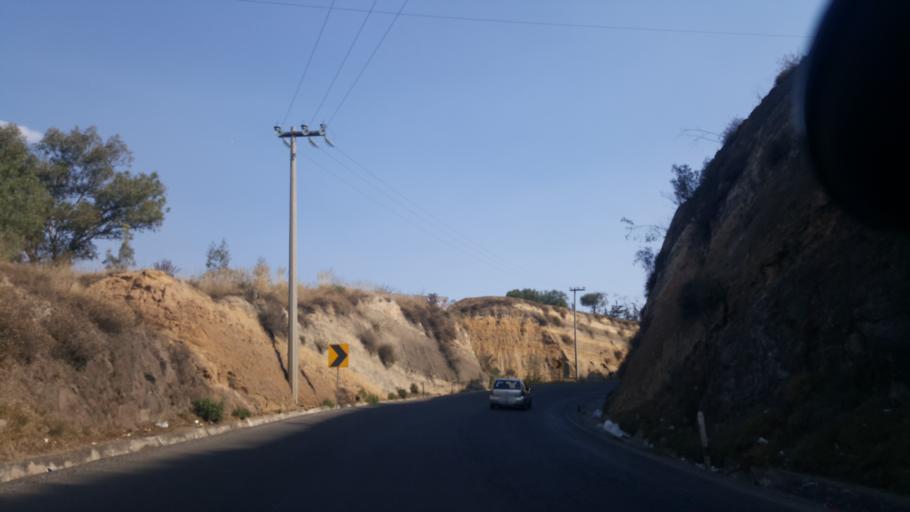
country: MX
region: Mexico
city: Ciudad Lopez Mateos
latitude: 19.5818
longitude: -99.2695
